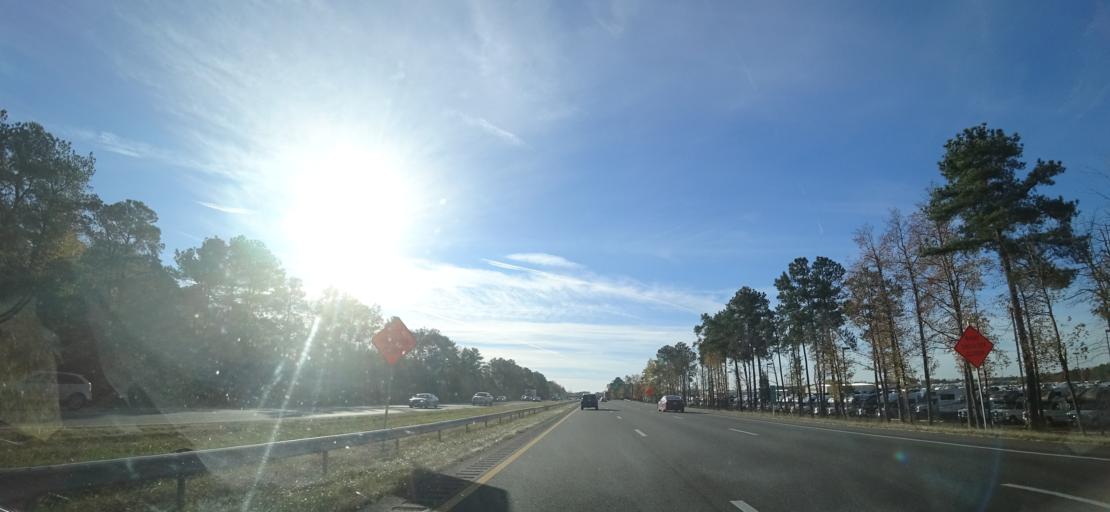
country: US
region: Virginia
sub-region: Hanover County
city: Ashland
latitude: 37.7279
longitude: -77.4509
